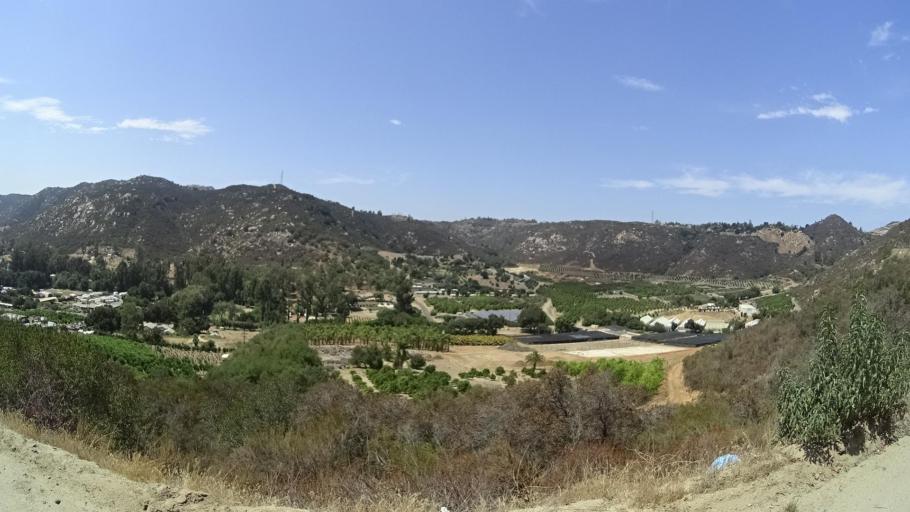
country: US
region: California
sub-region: San Diego County
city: Hidden Meadows
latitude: 33.2041
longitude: -117.0861
